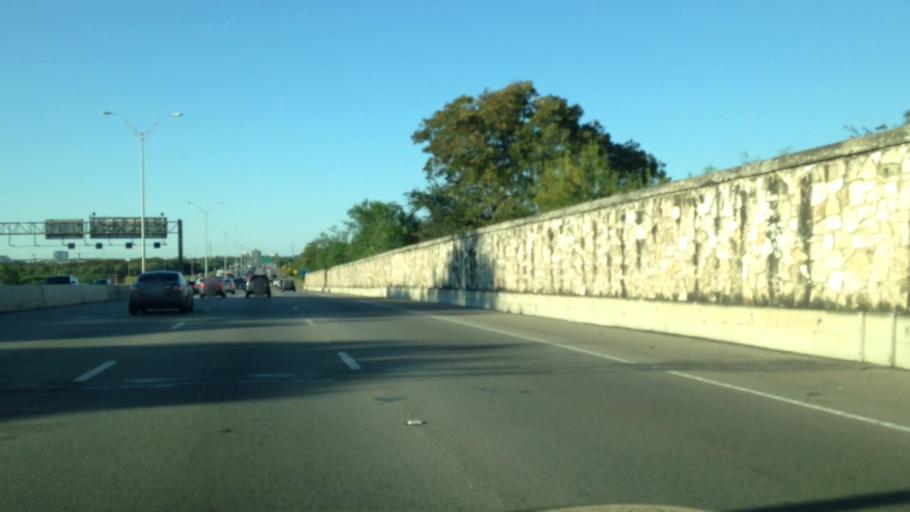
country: US
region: Texas
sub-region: Bexar County
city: Olmos Park
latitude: 29.4822
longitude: -98.4818
